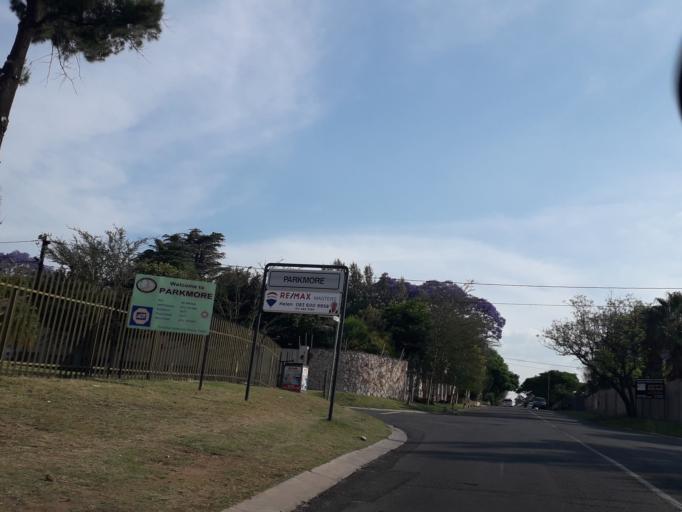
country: ZA
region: Gauteng
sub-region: City of Johannesburg Metropolitan Municipality
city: Johannesburg
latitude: -26.0922
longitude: 28.0394
